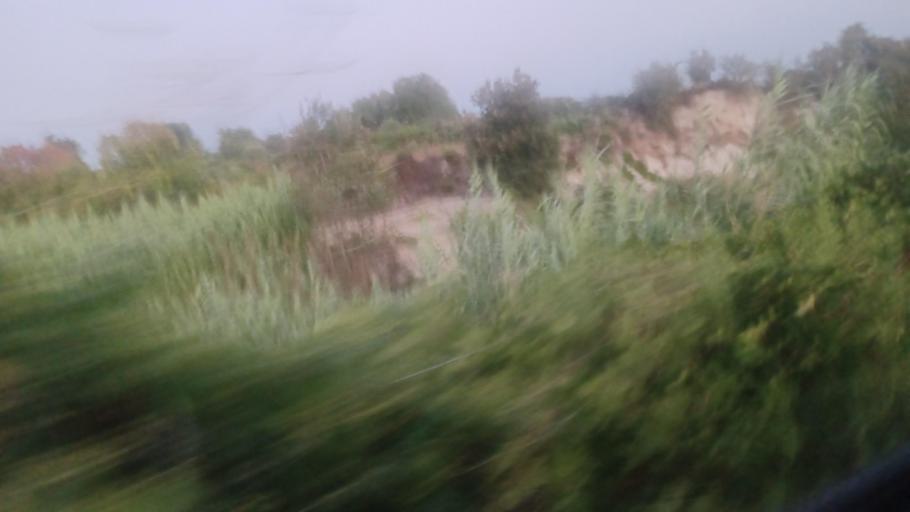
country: CY
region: Pafos
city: Tala
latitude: 34.8657
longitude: 32.4729
